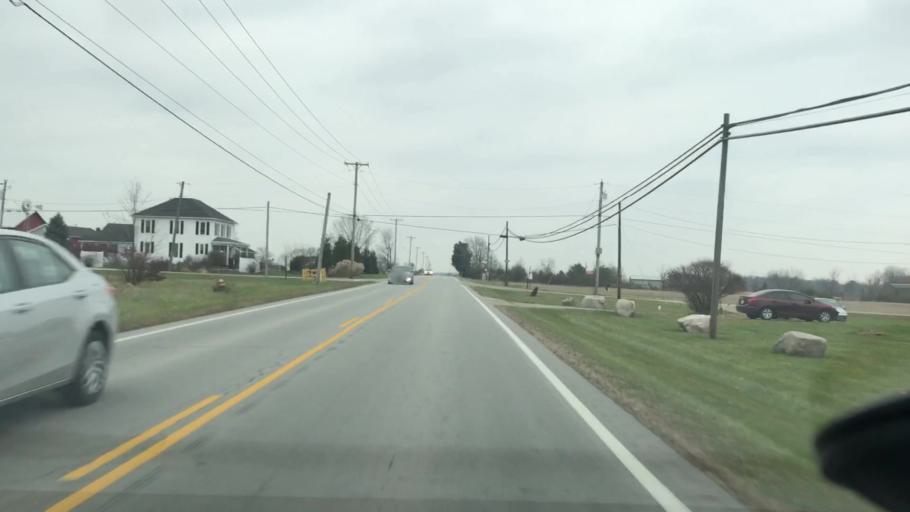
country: US
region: Ohio
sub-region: Greene County
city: Yellow Springs
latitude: 39.7928
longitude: -83.9471
